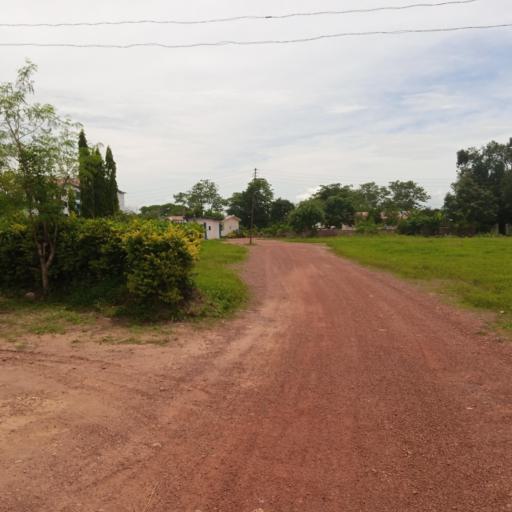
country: SL
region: Southern Province
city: Largo
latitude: 8.1114
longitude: -12.0791
